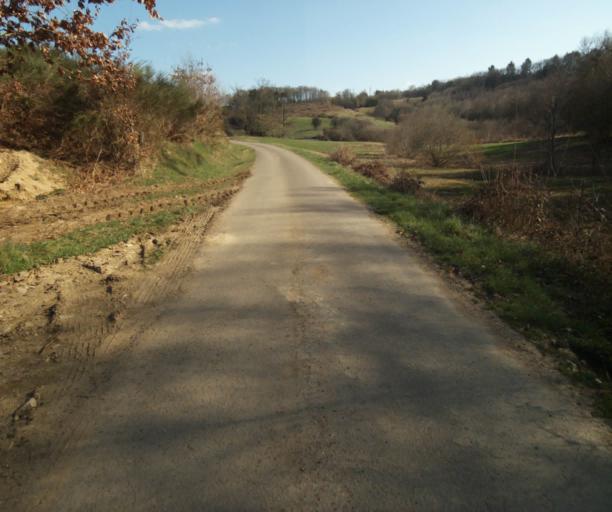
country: FR
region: Limousin
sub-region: Departement de la Correze
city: Saint-Mexant
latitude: 45.3232
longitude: 1.6171
